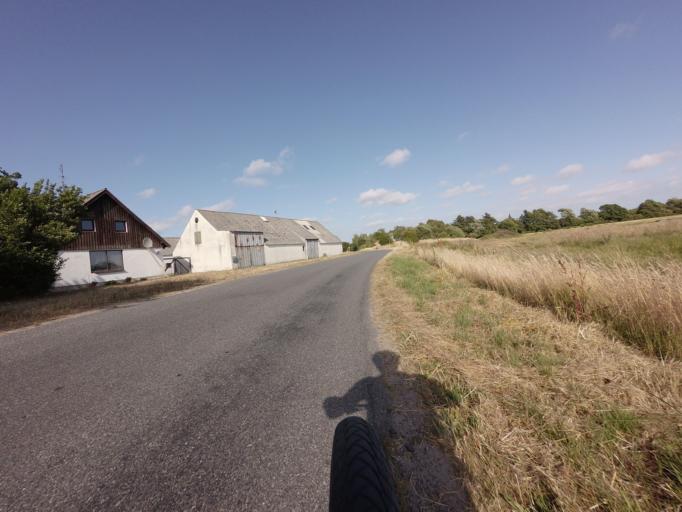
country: DK
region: North Denmark
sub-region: Laeso Kommune
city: Byrum
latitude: 57.2698
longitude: 10.9326
